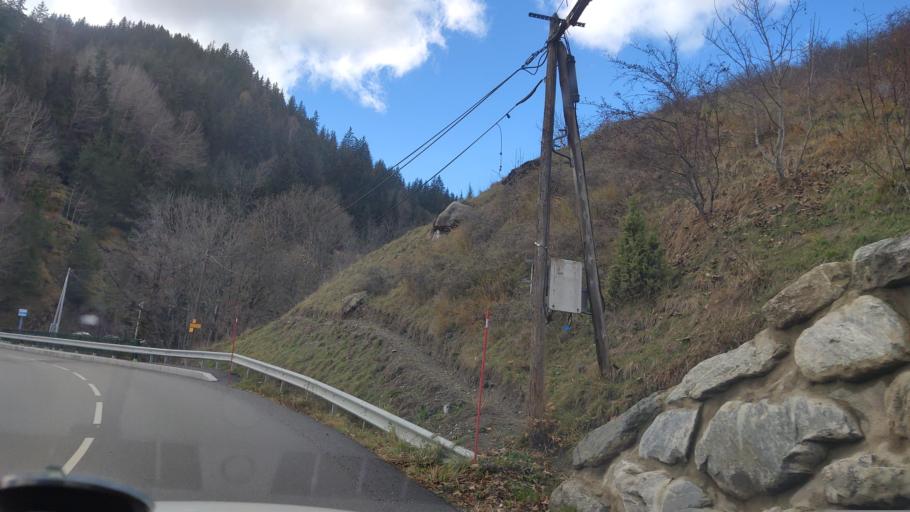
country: FR
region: Rhone-Alpes
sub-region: Departement de la Savoie
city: Saint-Jean-de-Maurienne
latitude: 45.1928
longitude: 6.2869
